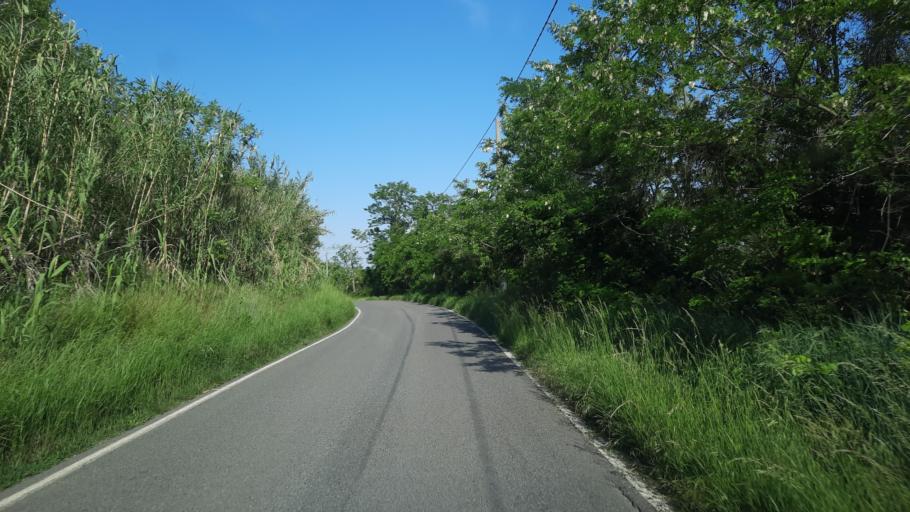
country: IT
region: Piedmont
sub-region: Provincia di Alessandria
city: San Giorgio Monferrato
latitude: 45.1196
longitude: 8.4212
